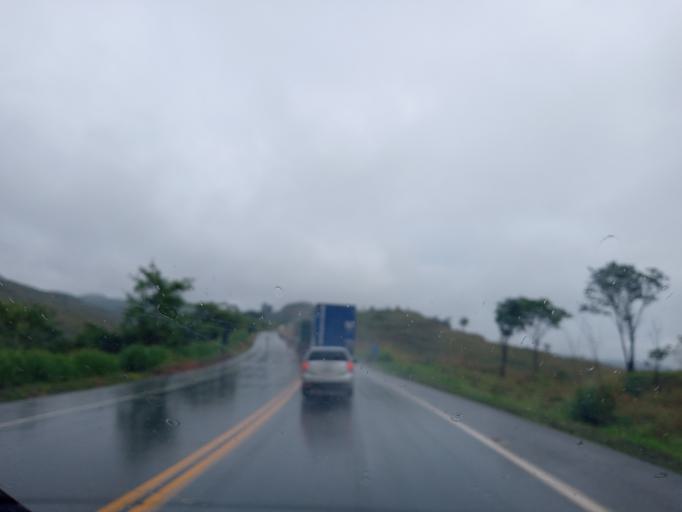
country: BR
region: Minas Gerais
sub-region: Luz
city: Luz
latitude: -19.7251
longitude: -45.8694
